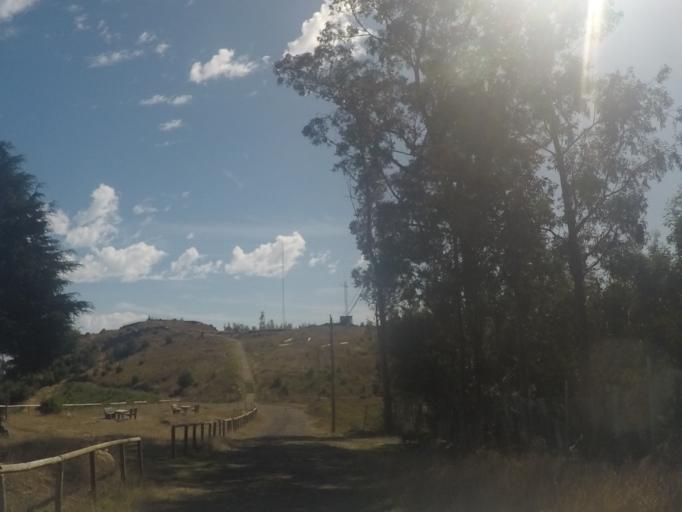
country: PT
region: Madeira
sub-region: Funchal
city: Nossa Senhora do Monte
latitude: 32.6949
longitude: -16.9042
